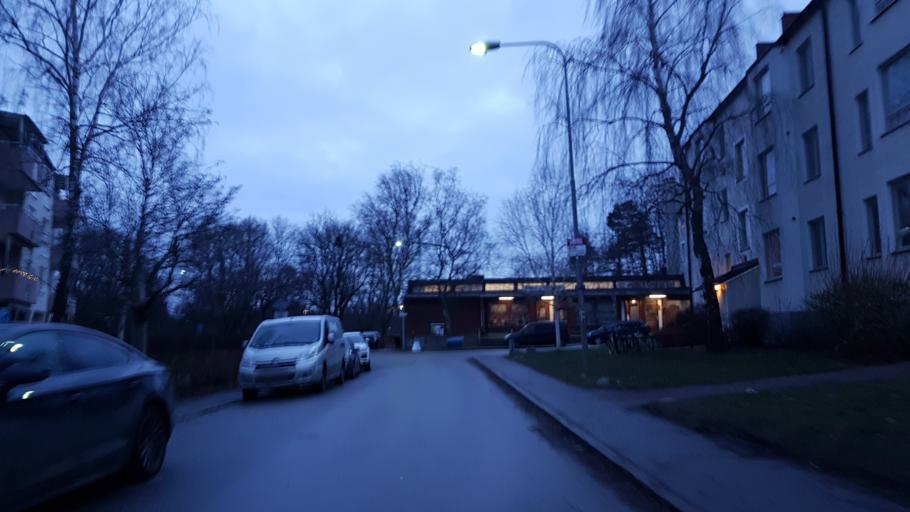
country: SE
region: Stockholm
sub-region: Stockholms Kommun
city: Arsta
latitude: 59.2723
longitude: 18.0532
